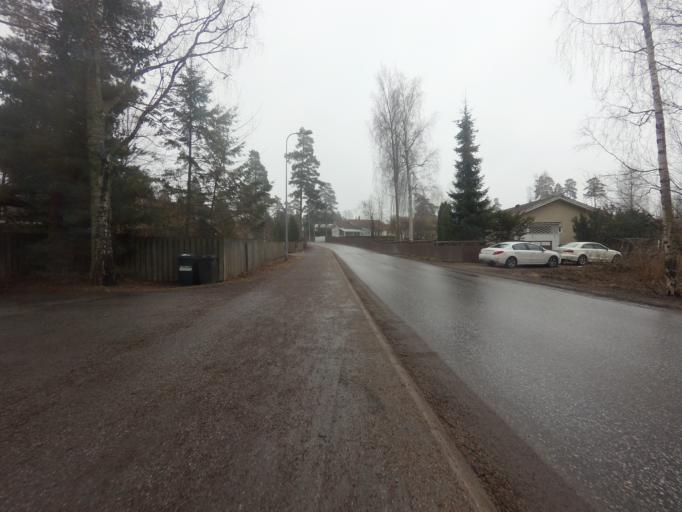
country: FI
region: Uusimaa
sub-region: Helsinki
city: Koukkuniemi
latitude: 60.1501
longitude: 24.7015
